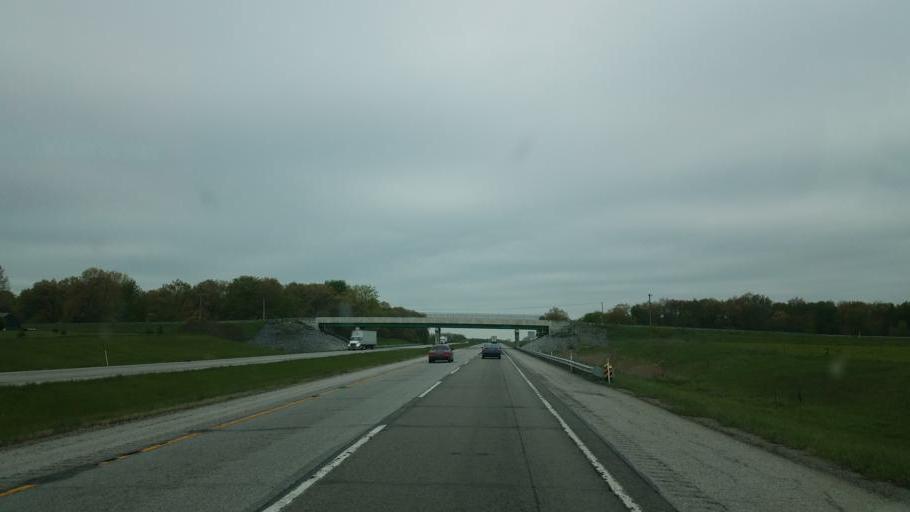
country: US
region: Michigan
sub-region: Saint Joseph County
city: White Pigeon
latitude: 41.7525
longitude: -85.5997
